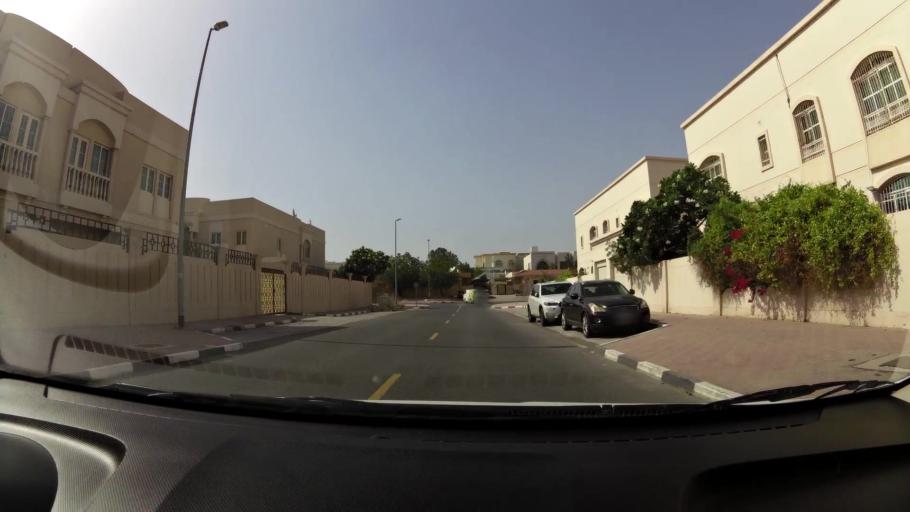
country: AE
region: Ash Shariqah
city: Sharjah
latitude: 25.2400
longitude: 55.3487
